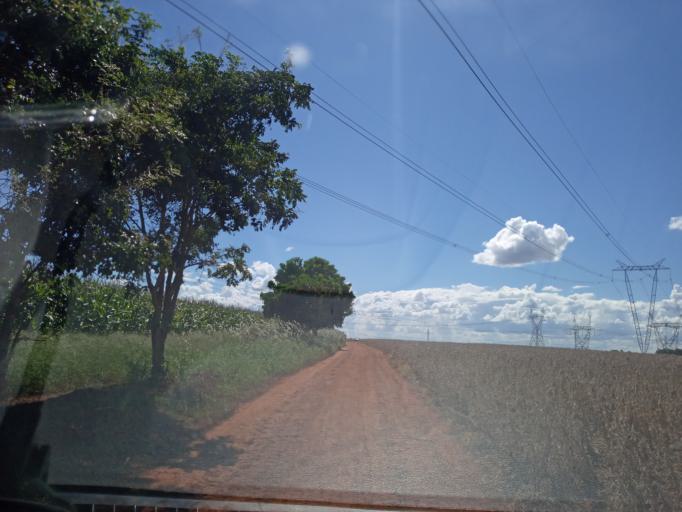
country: BR
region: Goias
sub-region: Itumbiara
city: Itumbiara
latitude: -18.4355
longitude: -49.1194
